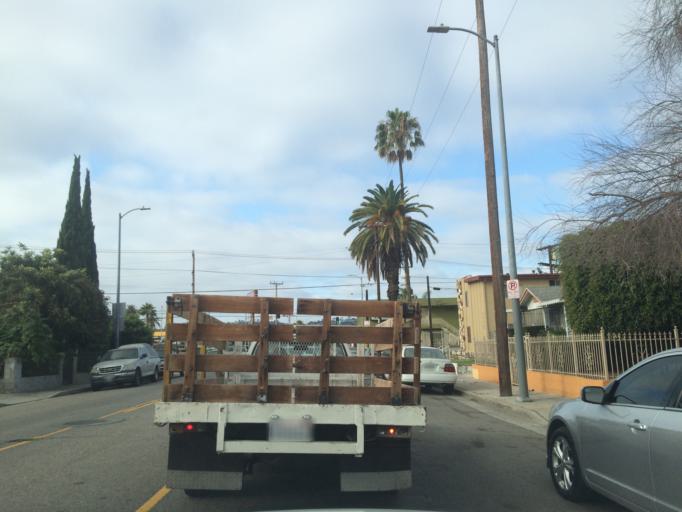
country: US
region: California
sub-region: Los Angeles County
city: View Park-Windsor Hills
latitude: 34.0335
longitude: -118.3559
